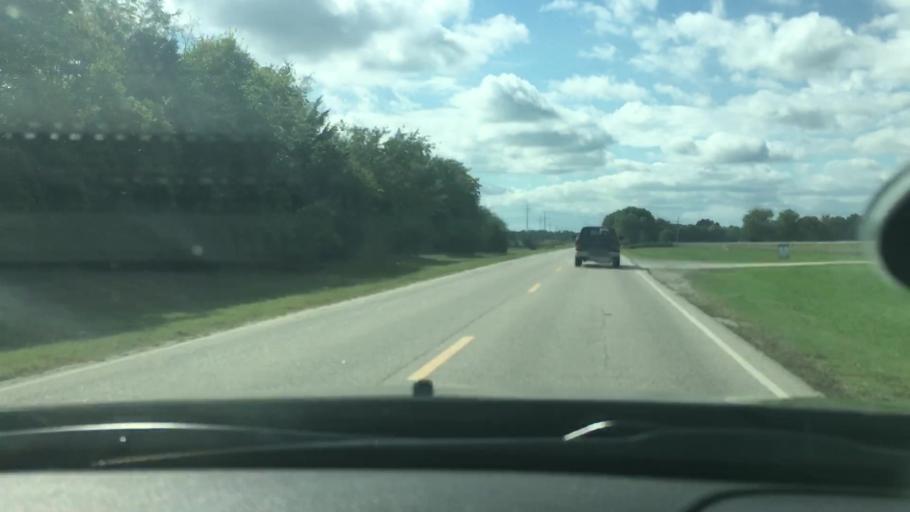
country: US
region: Oklahoma
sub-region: Pontotoc County
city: Ada
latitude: 34.6975
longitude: -96.6349
